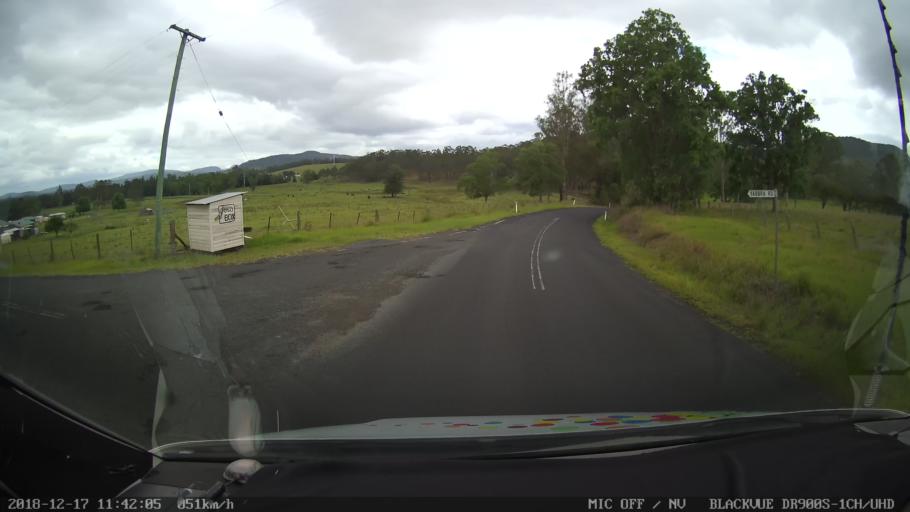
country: AU
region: New South Wales
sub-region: Kyogle
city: Kyogle
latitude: -28.6701
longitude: 152.5882
